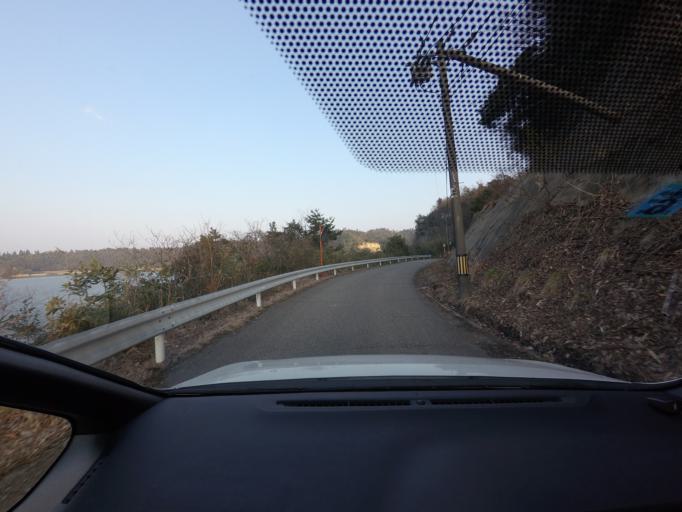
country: JP
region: Ishikawa
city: Nanao
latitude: 37.1443
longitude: 137.0169
